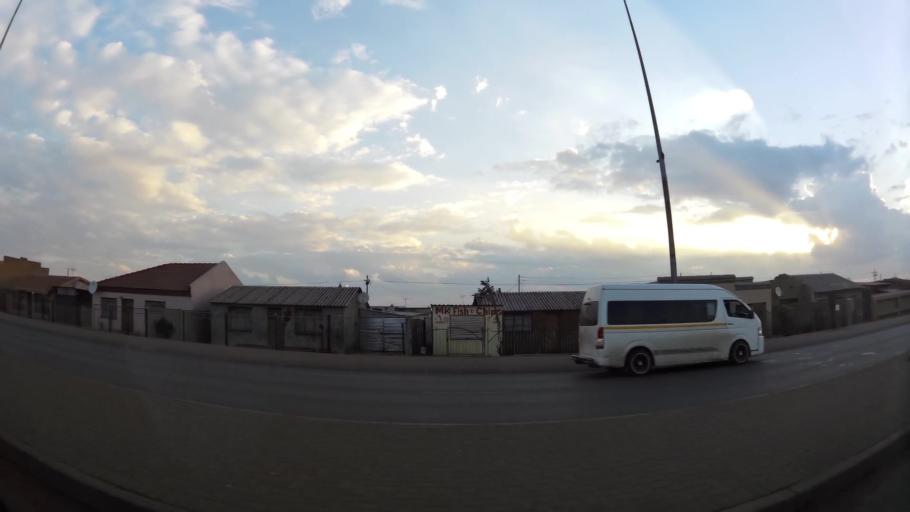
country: ZA
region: Gauteng
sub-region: City of Johannesburg Metropolitan Municipality
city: Orange Farm
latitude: -26.5702
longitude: 27.8373
